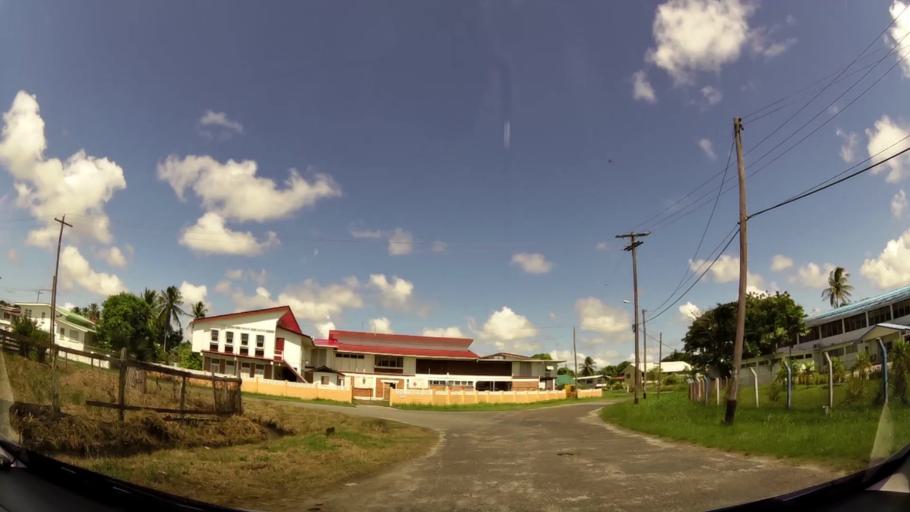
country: GY
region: Demerara-Mahaica
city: Georgetown
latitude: 6.7991
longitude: -58.1362
